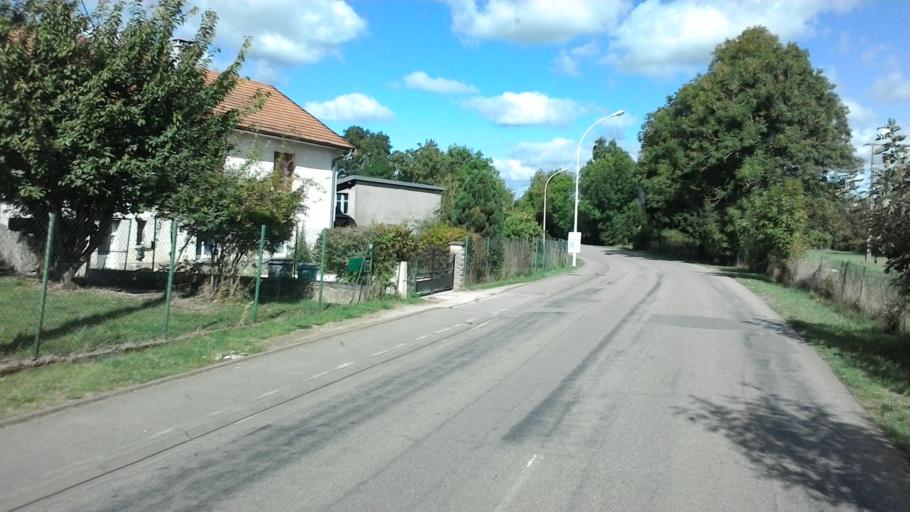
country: FR
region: Lorraine
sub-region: Departement des Vosges
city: Neufchateau
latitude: 48.3596
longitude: 5.6828
